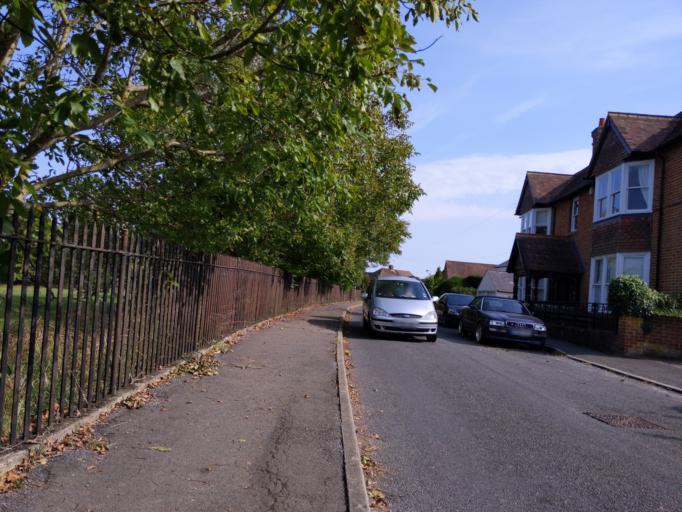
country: GB
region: England
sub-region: Oxfordshire
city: Radley
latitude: 51.7117
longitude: -1.2277
